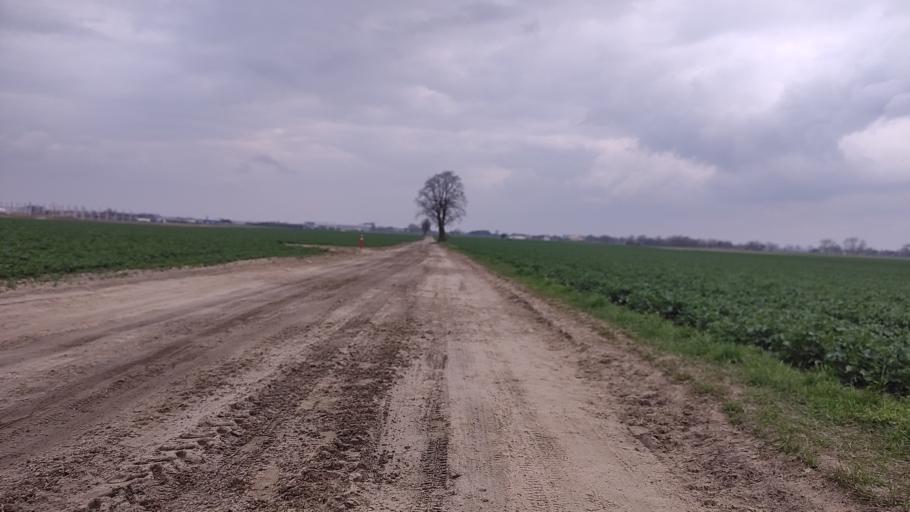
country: PL
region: Greater Poland Voivodeship
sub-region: Powiat poznanski
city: Kleszczewo
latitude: 52.4026
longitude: 17.1553
